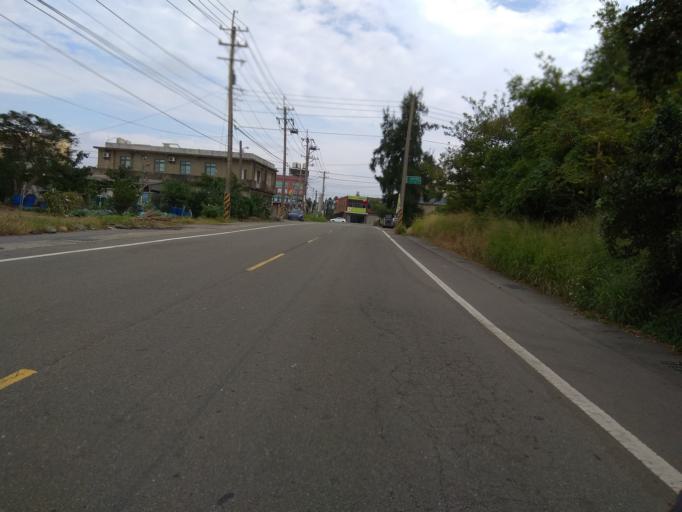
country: TW
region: Taiwan
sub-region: Hsinchu
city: Zhubei
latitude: 24.9865
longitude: 121.0418
